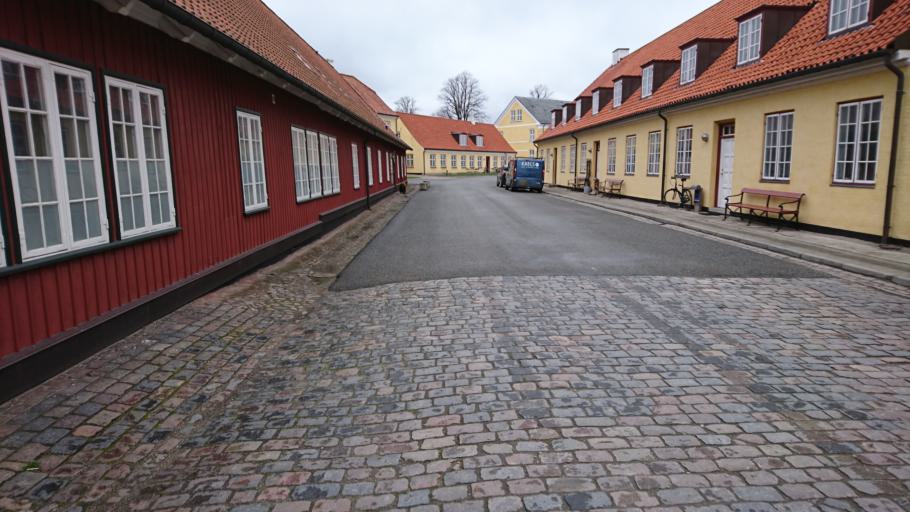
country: DK
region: Capital Region
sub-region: Helsingor Kommune
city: Helsingor
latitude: 56.0379
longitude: 12.6210
